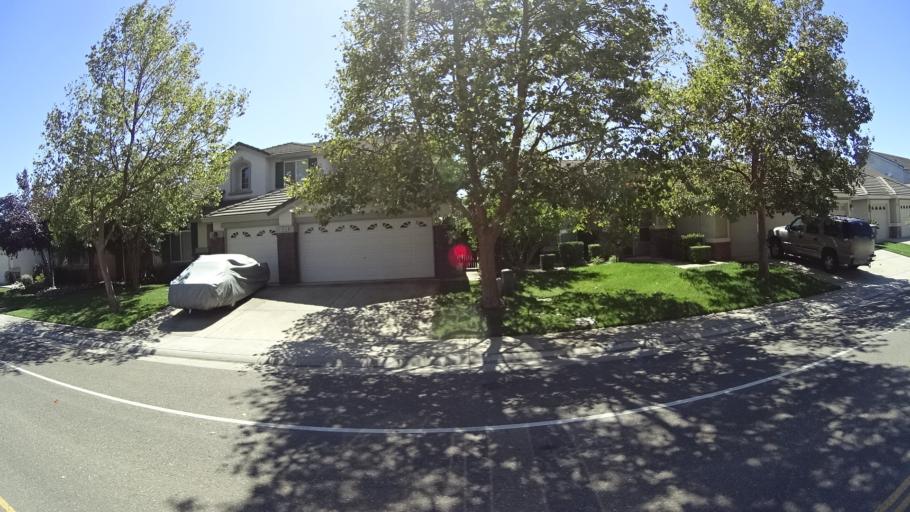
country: US
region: California
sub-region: Sacramento County
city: Elk Grove
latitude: 38.4022
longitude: -121.3450
